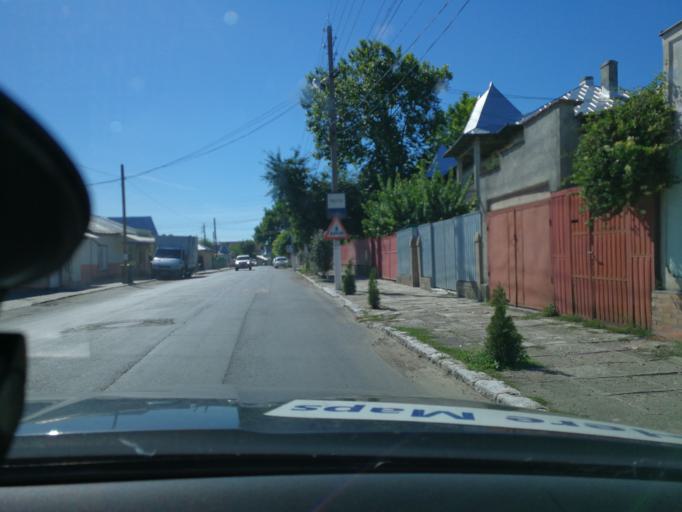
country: RO
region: Tulcea
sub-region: Oras Macin
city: Macin
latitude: 45.2432
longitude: 28.1375
